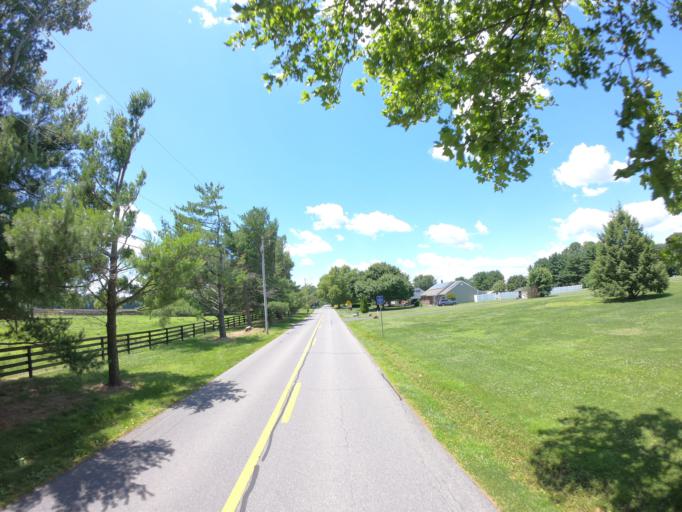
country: US
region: Delaware
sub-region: New Castle County
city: Middletown
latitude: 39.4799
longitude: -75.7373
